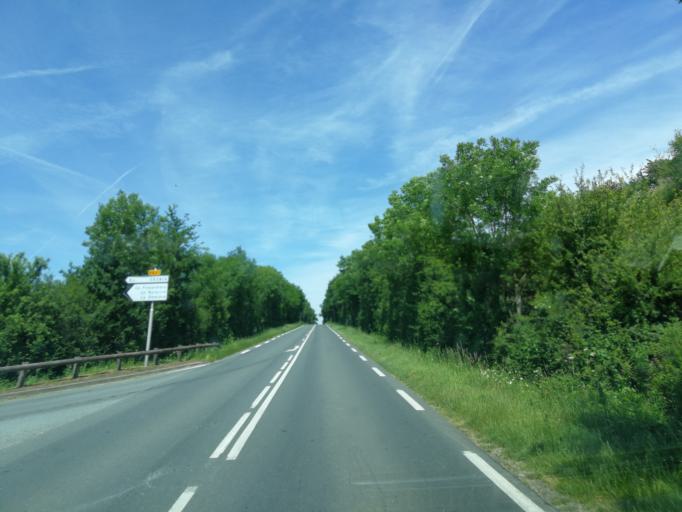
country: FR
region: Pays de la Loire
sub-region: Departement de la Vendee
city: Antigny
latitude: 46.6052
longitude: -0.7885
